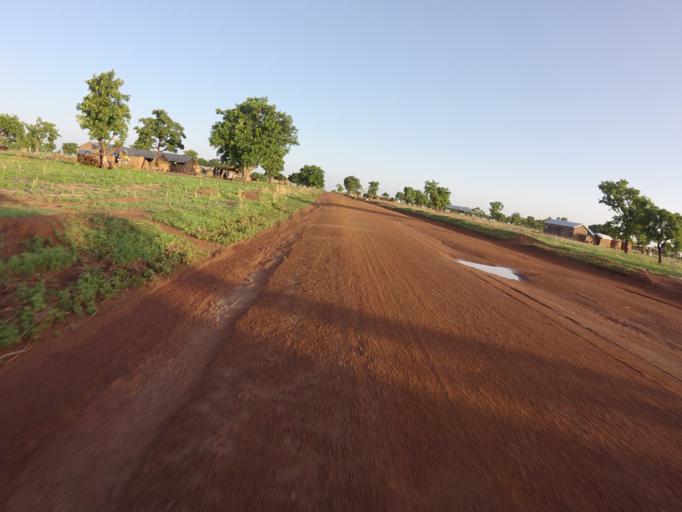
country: TG
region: Savanes
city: Sansanne-Mango
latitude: 10.2653
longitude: -0.0805
